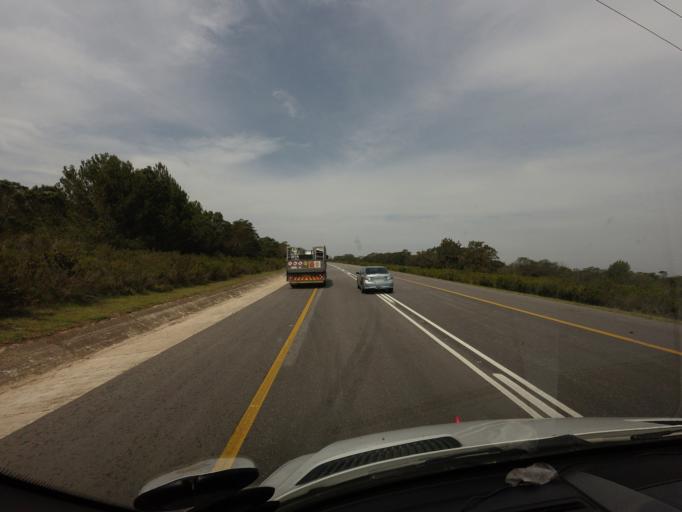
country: ZA
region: Eastern Cape
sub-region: Cacadu District Municipality
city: Kruisfontein
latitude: -33.9956
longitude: 24.7091
